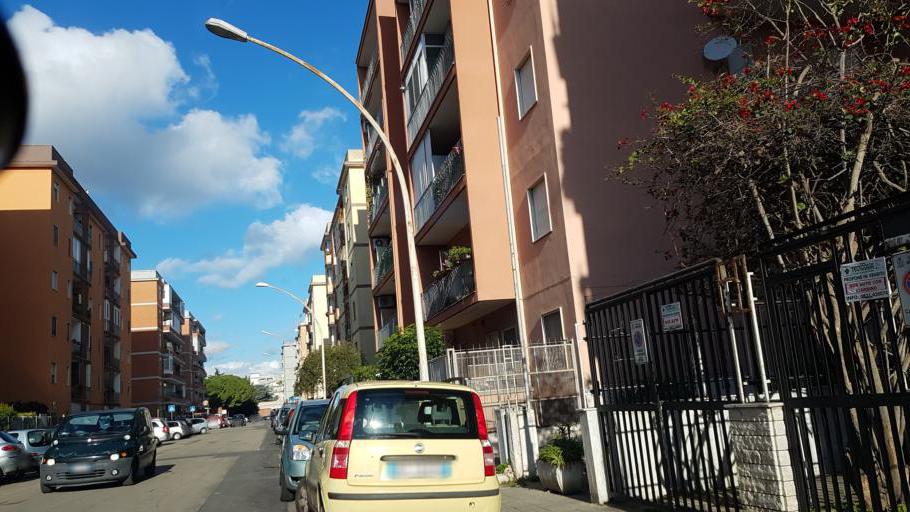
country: IT
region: Apulia
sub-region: Provincia di Brindisi
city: Brindisi
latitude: 40.6259
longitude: 17.9267
